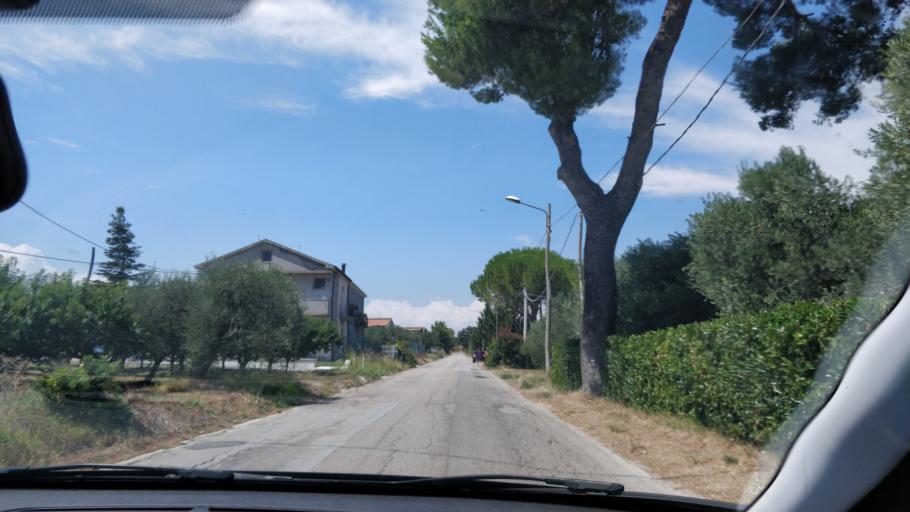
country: IT
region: Abruzzo
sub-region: Provincia di Chieti
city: Francavilla al Mare
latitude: 42.4231
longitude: 14.2619
